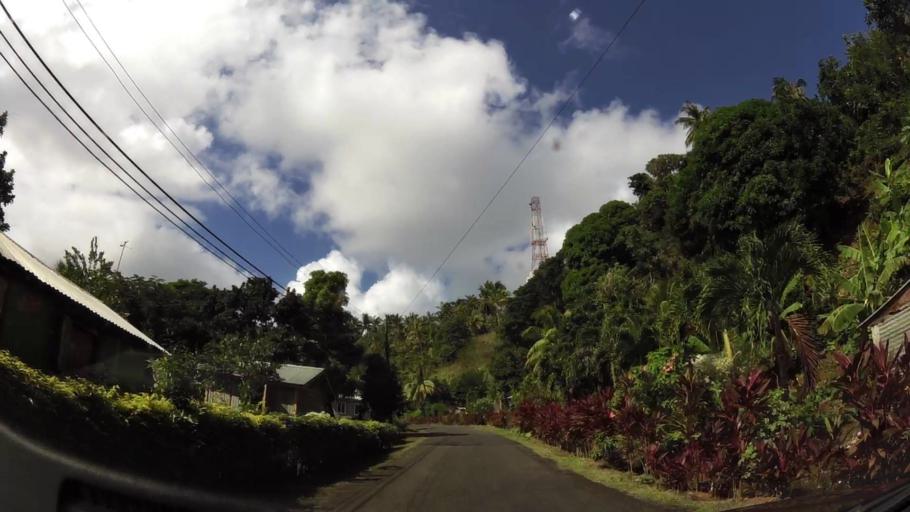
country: DM
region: Saint David
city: Castle Bruce
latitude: 15.4885
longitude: -61.2538
